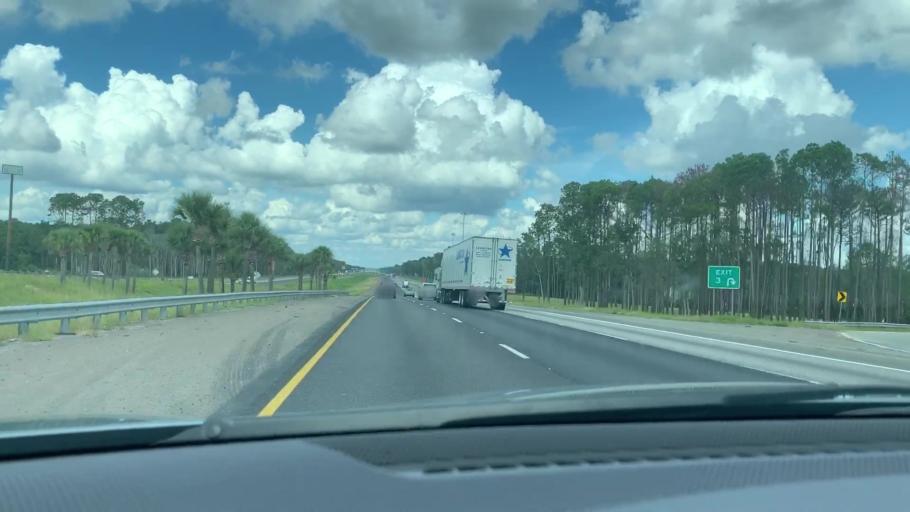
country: US
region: Georgia
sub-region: Camden County
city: Kingsland
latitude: 30.7915
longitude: -81.6589
